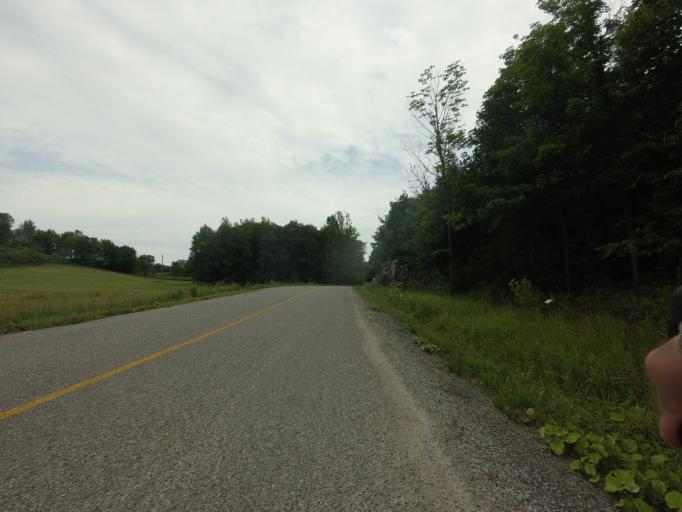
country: CA
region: Ontario
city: Kingston
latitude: 44.5976
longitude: -76.6403
